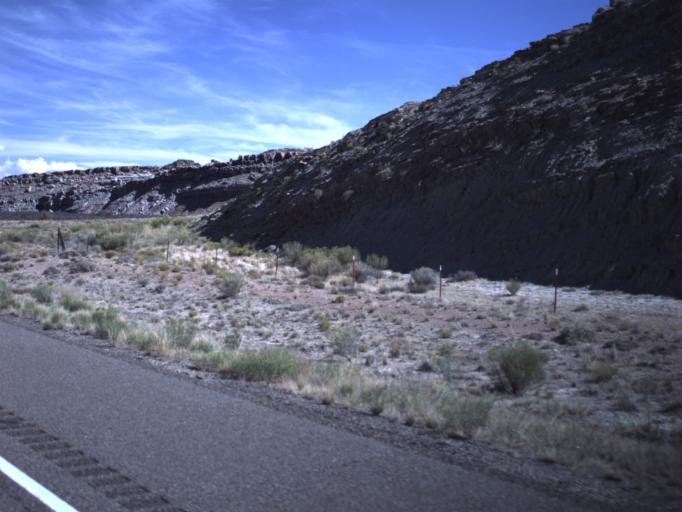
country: US
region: Utah
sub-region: Carbon County
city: East Carbon City
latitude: 38.9245
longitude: -110.4123
